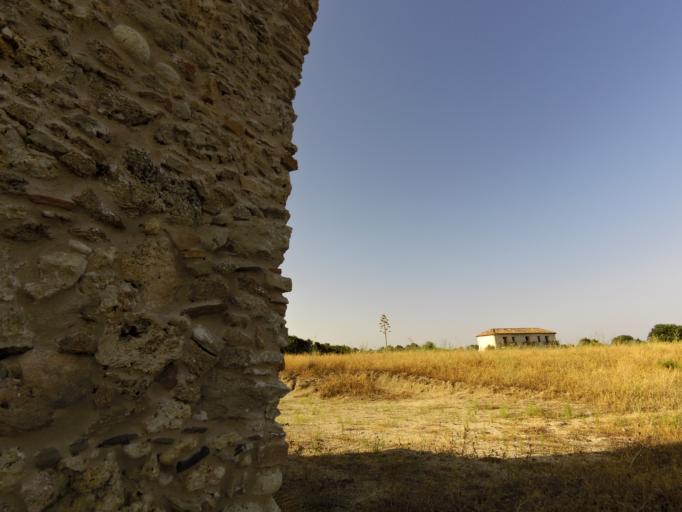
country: IT
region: Calabria
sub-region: Provincia di Reggio Calabria
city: Caulonia Marina
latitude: 38.3712
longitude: 16.4947
